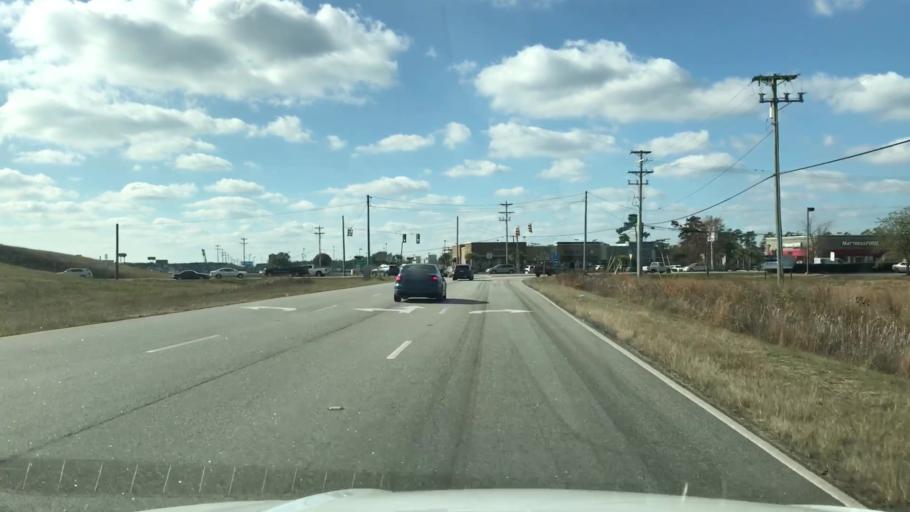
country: US
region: South Carolina
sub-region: Horry County
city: Socastee
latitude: 33.6515
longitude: -78.9812
